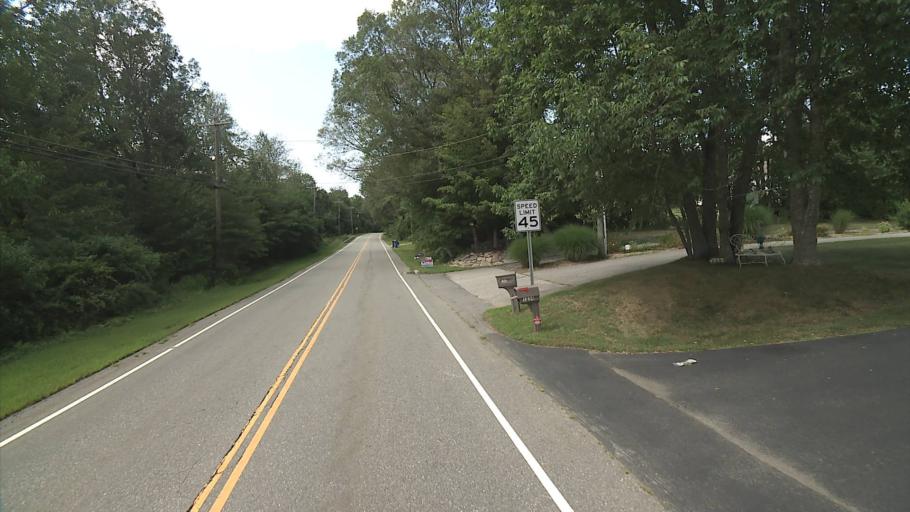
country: US
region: Connecticut
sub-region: New London County
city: Colchester
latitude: 41.6203
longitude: -72.2759
